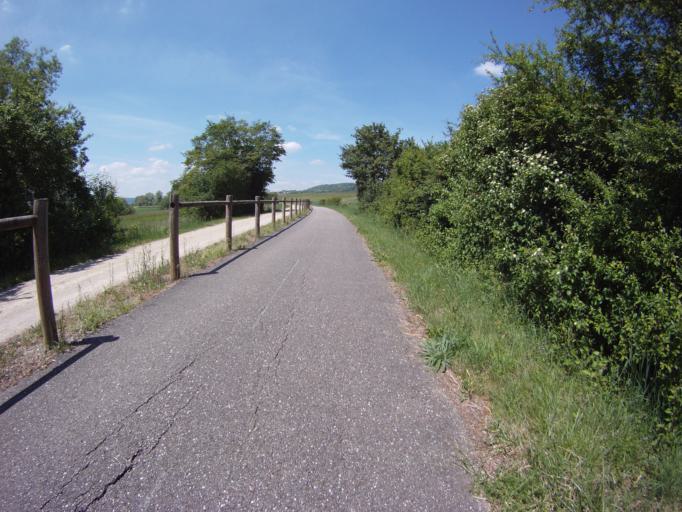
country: FR
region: Lorraine
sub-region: Departement de Meurthe-et-Moselle
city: Champenoux
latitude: 48.7415
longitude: 6.3041
